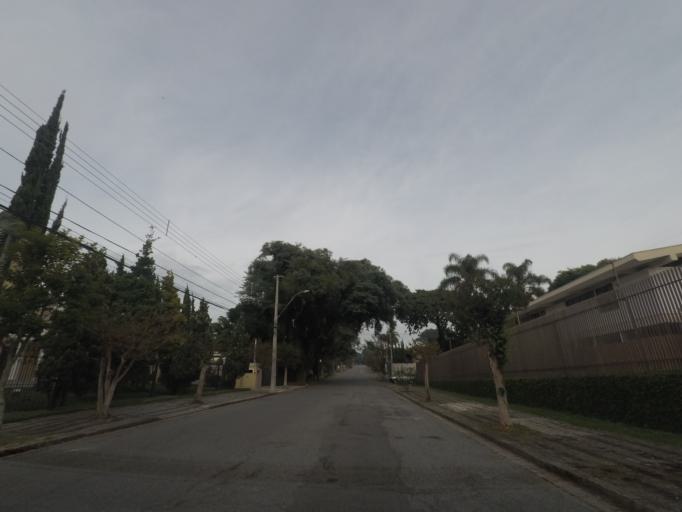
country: BR
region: Parana
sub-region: Curitiba
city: Curitiba
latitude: -25.4413
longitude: -49.2942
